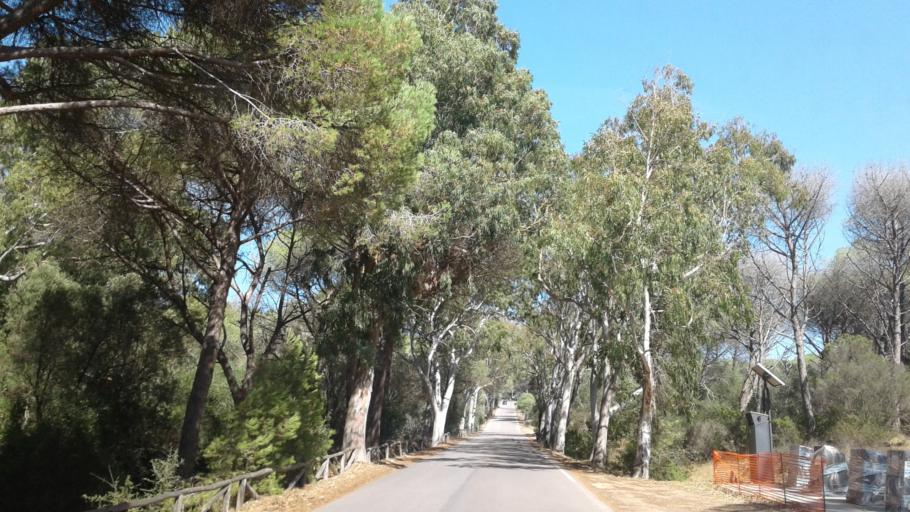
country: IT
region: Sardinia
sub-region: Provincia di Olbia-Tempio
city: La Maddalena
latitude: 41.2106
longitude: 9.4562
